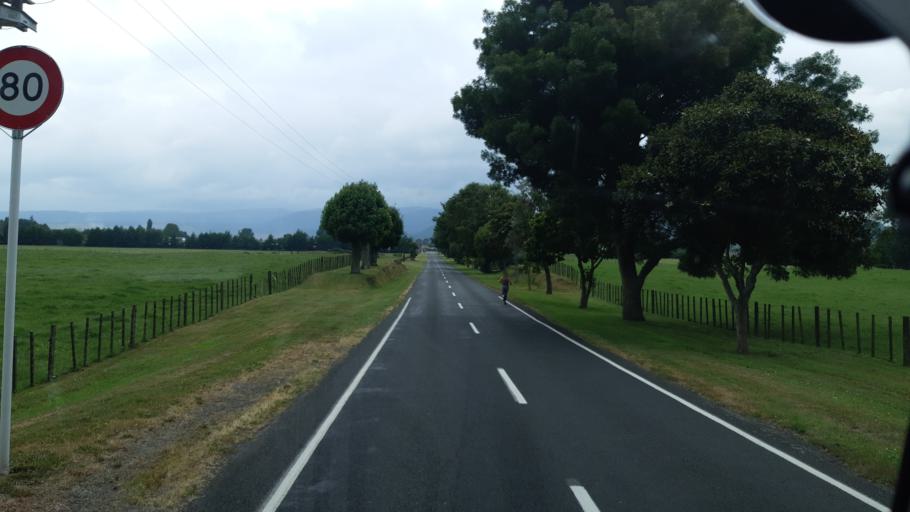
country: NZ
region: Waikato
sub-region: South Waikato District
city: Tokoroa
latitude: -38.3750
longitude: 175.7630
